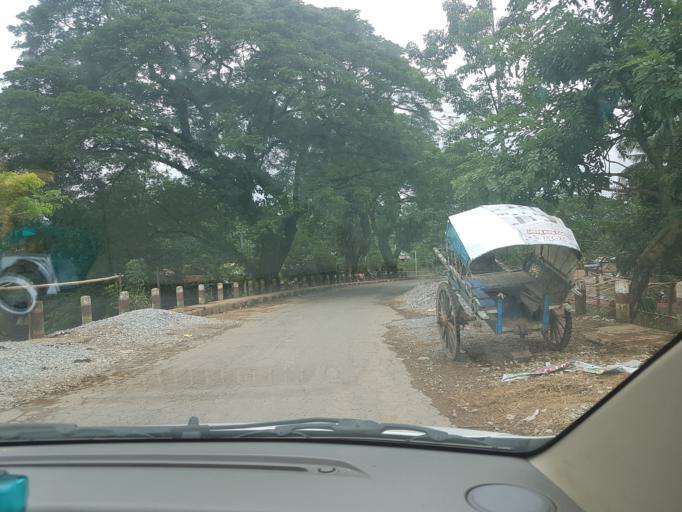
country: MM
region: Bago
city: Nyaunglebin
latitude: 17.9172
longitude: 96.8500
